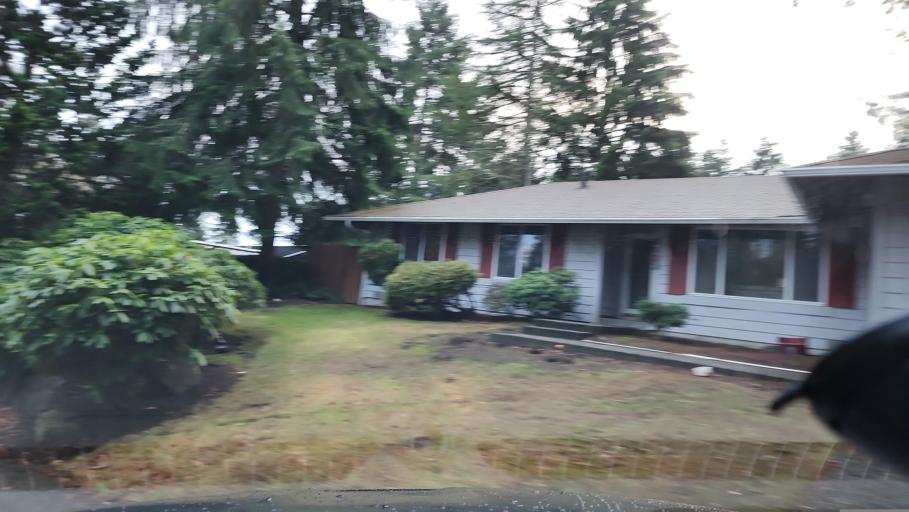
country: US
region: Washington
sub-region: King County
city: Redmond
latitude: 47.6808
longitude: -122.1060
